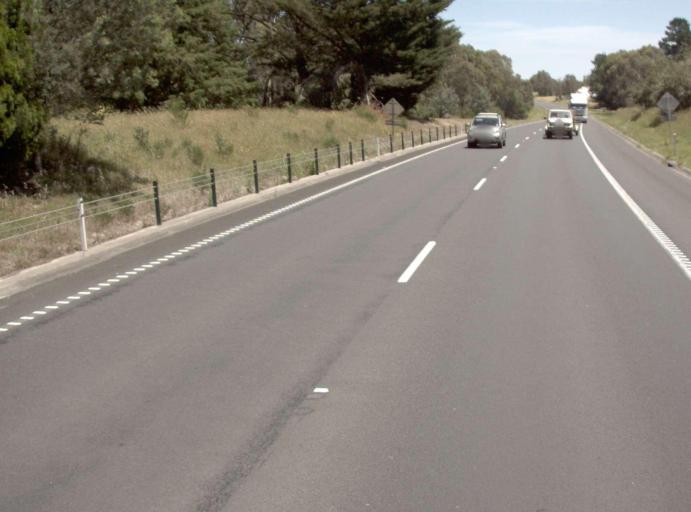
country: AU
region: Victoria
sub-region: Cardinia
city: Garfield
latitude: -38.0779
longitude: 145.6837
